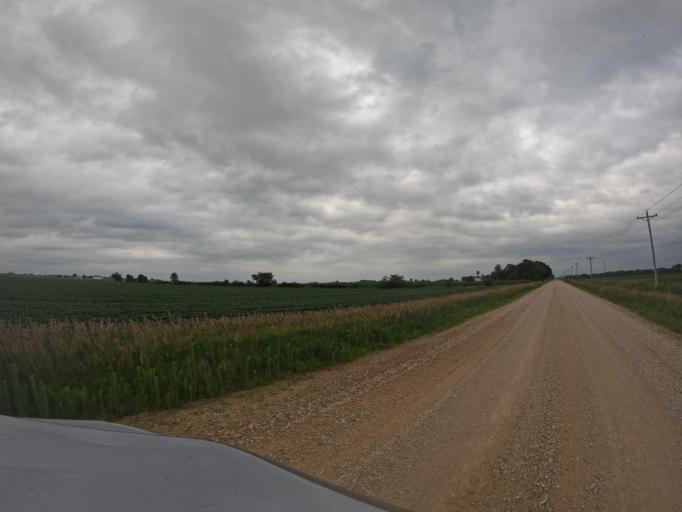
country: US
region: Iowa
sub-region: Clinton County
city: De Witt
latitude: 41.7864
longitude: -90.4385
